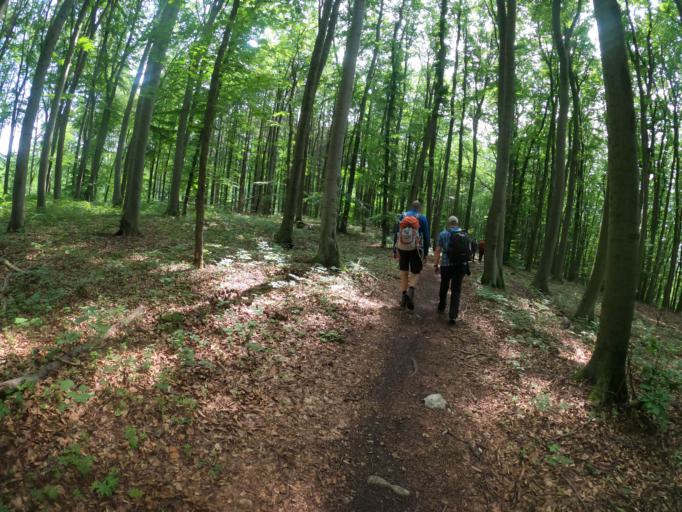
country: DE
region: Bavaria
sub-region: Upper Franconia
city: Litzendorf
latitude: 49.9289
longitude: 11.0468
